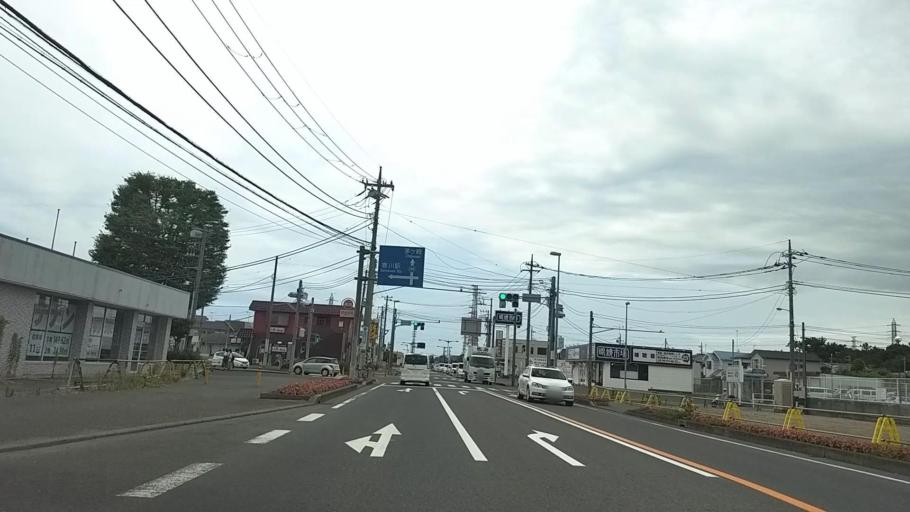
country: JP
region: Kanagawa
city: Chigasaki
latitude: 35.3729
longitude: 139.3832
